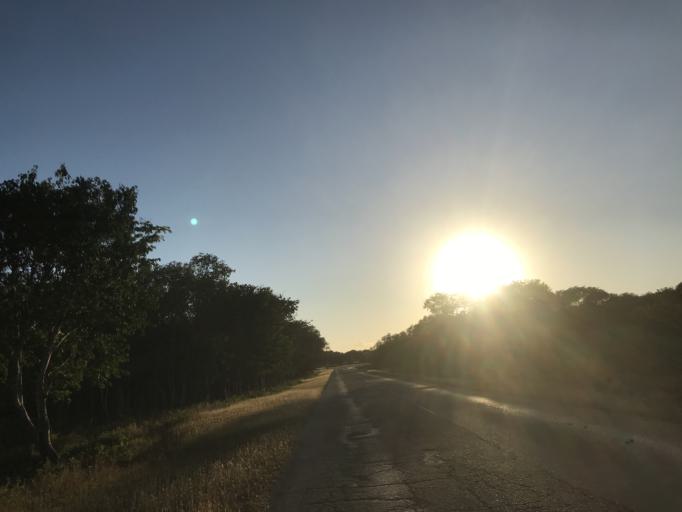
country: CU
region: Cienfuegos
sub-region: Municipio de Aguada de Pasajeros
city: Aguada de Pasajeros
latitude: 22.0688
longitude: -81.0394
